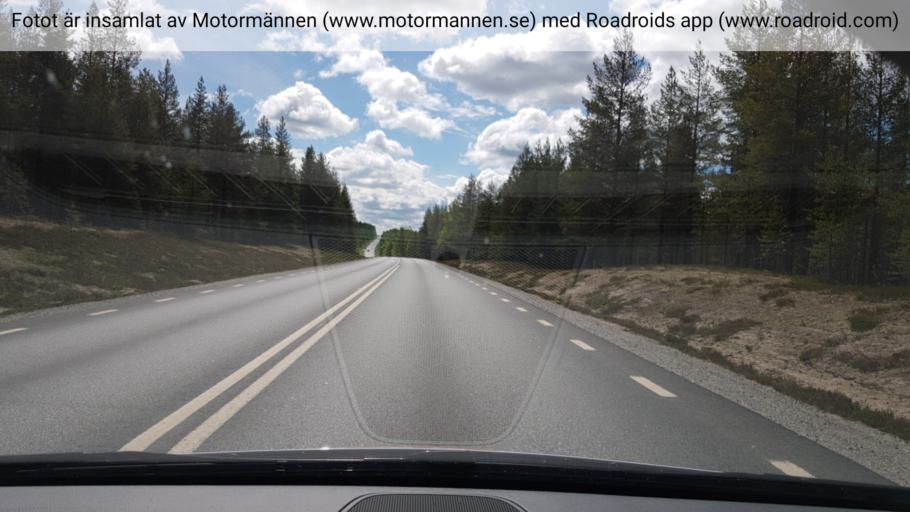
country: SE
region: Vaesterbotten
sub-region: Vannas Kommun
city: Vannasby
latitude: 64.0637
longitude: 19.9924
